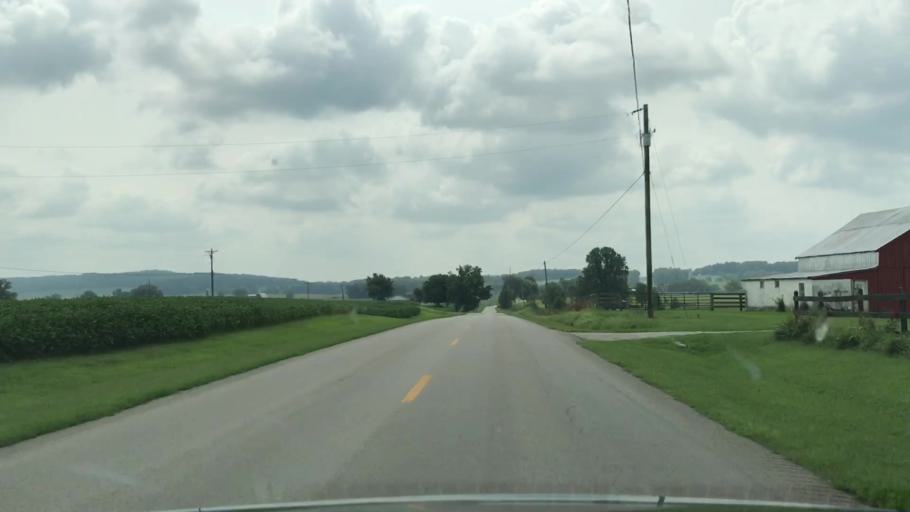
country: US
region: Kentucky
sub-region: Barren County
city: Cave City
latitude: 37.1032
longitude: -85.9784
